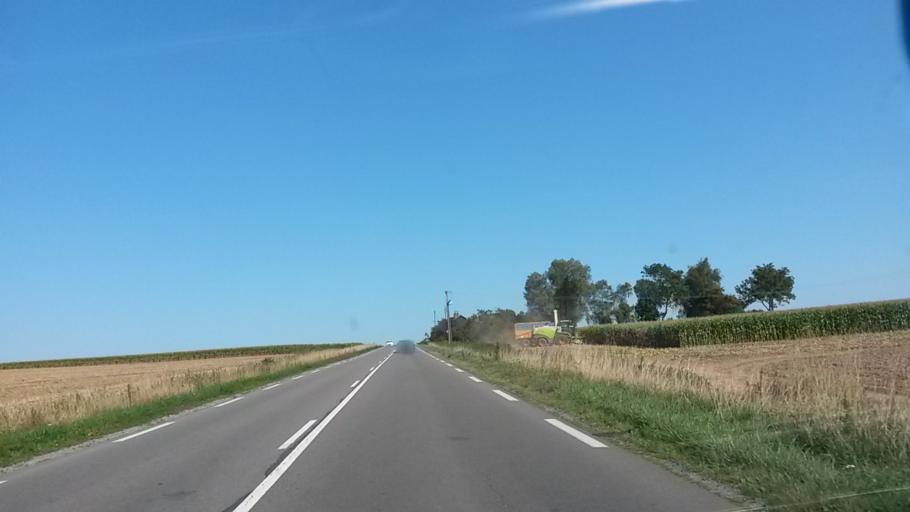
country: FR
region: Nord-Pas-de-Calais
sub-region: Departement du Nord
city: Avesnelles
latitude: 50.1847
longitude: 3.9520
